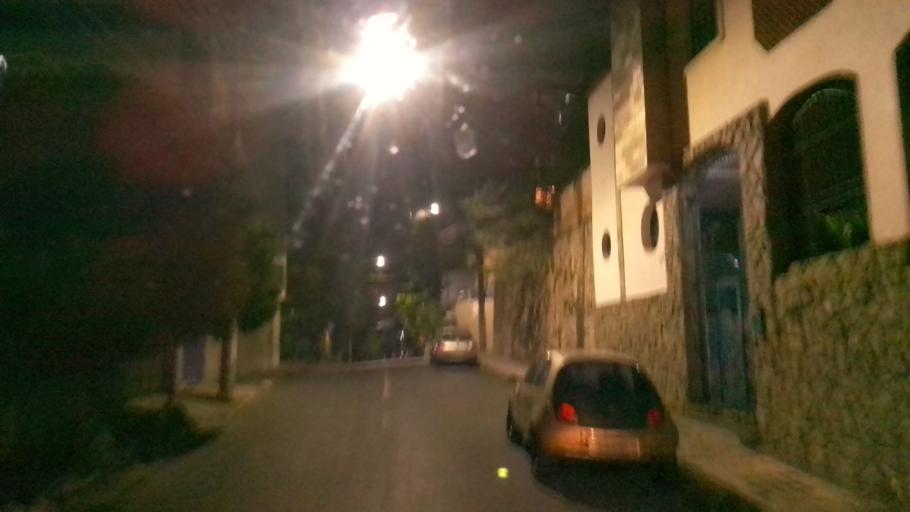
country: BR
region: Minas Gerais
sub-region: Belo Horizonte
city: Belo Horizonte
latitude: -19.9057
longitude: -43.9287
